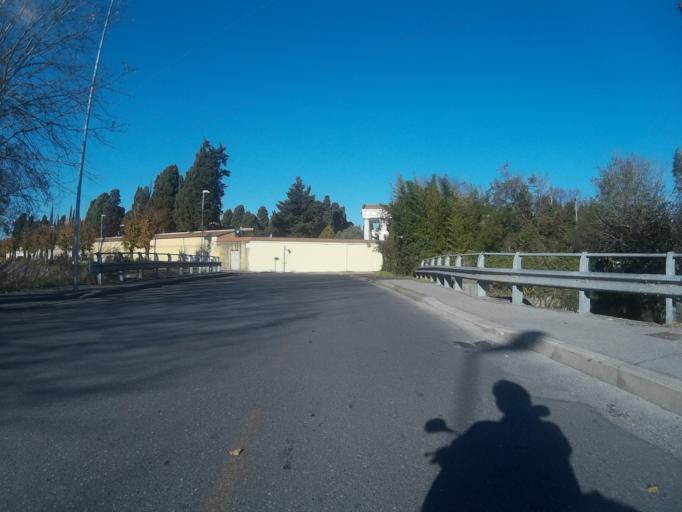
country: IT
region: Tuscany
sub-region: Provincia di Livorno
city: Livorno
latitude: 43.5675
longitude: 10.3272
